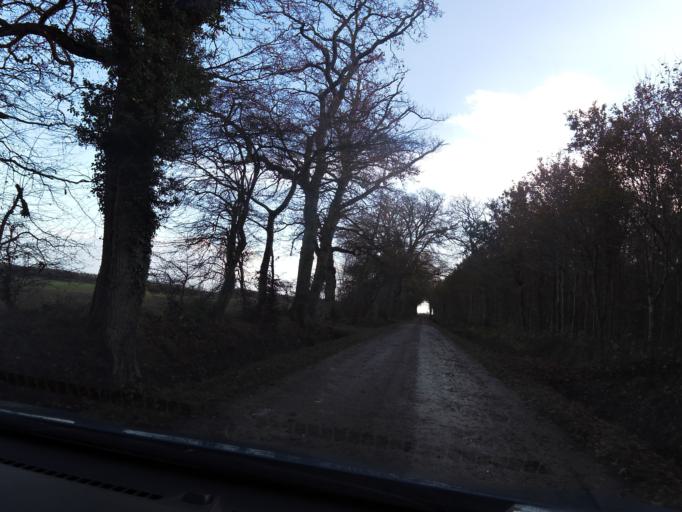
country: DK
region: Central Jutland
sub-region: Odder Kommune
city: Odder
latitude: 55.8550
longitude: 10.1643
